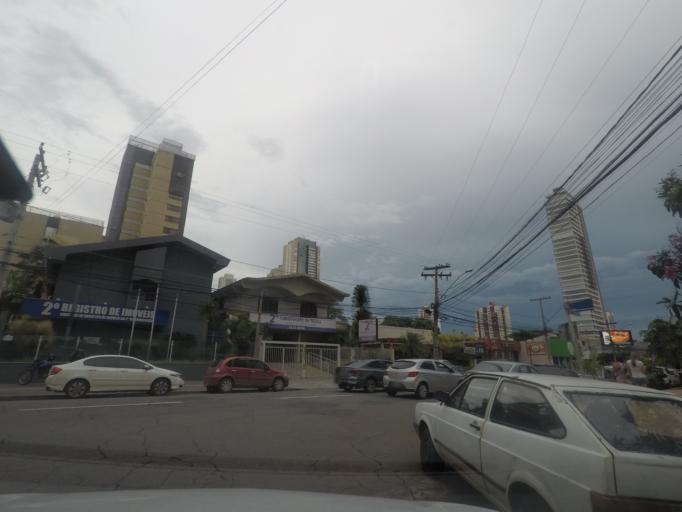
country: BR
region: Goias
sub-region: Goiania
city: Goiania
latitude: -16.6890
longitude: -49.2657
